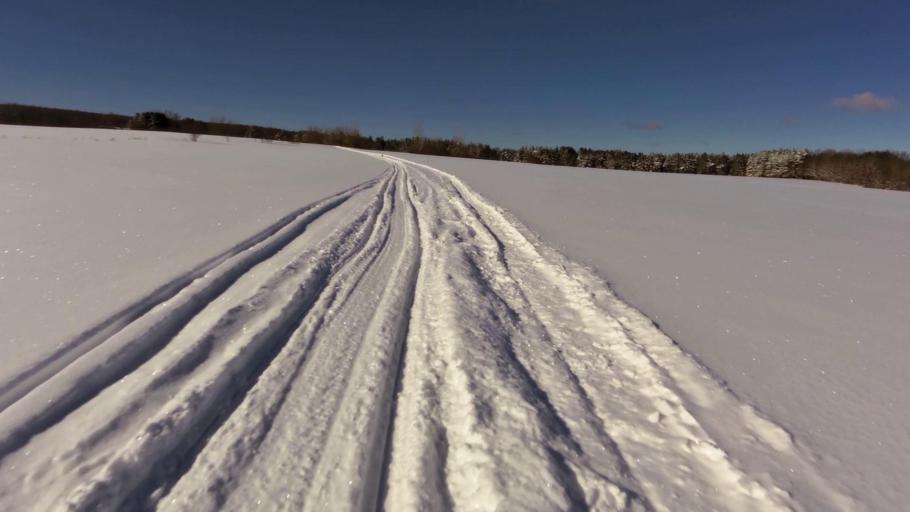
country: US
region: New York
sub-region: Chautauqua County
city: Silver Creek
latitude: 42.3520
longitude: -79.1355
